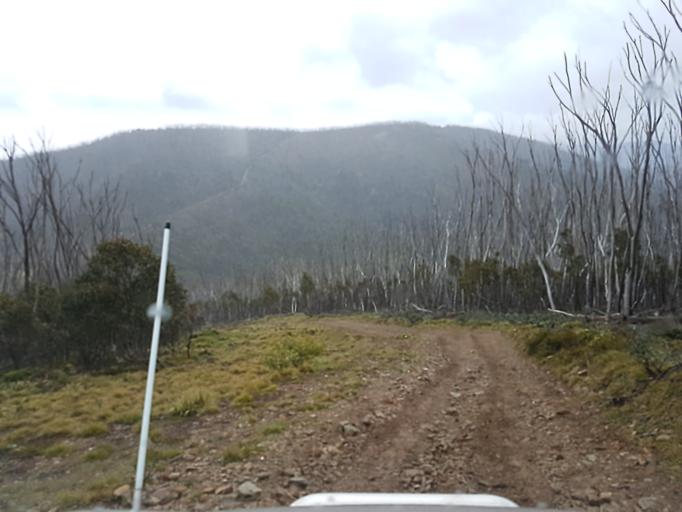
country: AU
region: Victoria
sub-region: Alpine
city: Mount Beauty
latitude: -37.0890
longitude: 147.1015
